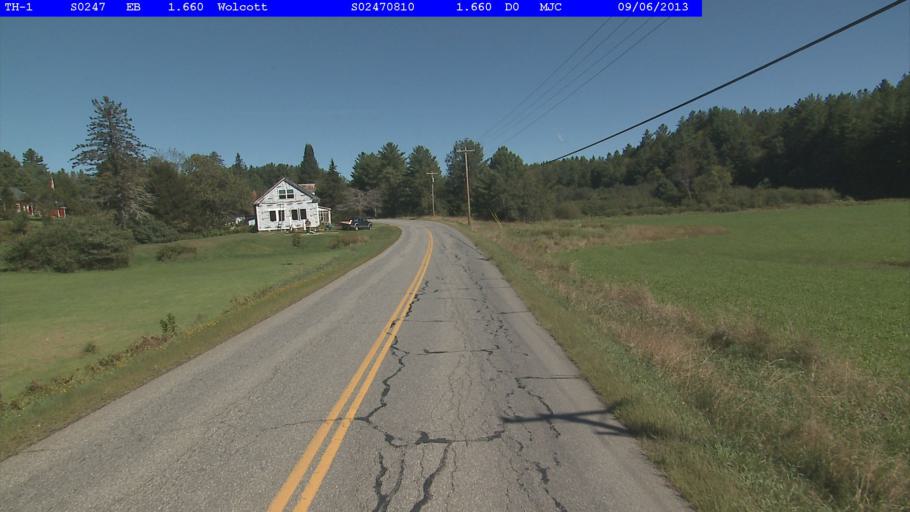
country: US
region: Vermont
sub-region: Lamoille County
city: Morrisville
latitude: 44.5797
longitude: -72.4758
